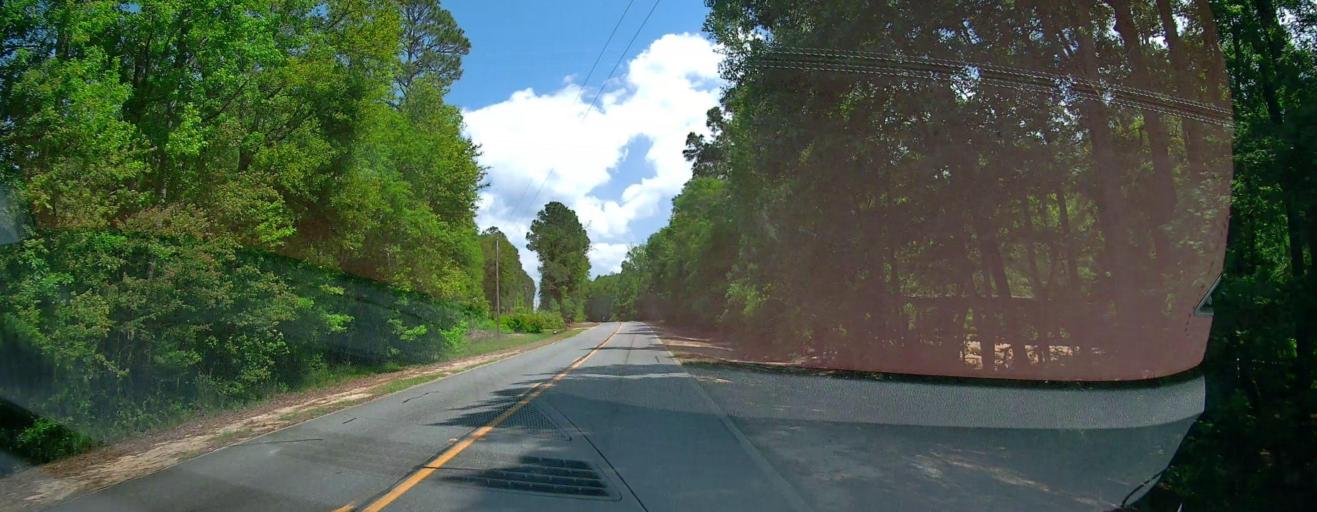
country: US
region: Georgia
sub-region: Treutlen County
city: Soperton
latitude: 32.5103
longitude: -82.6429
